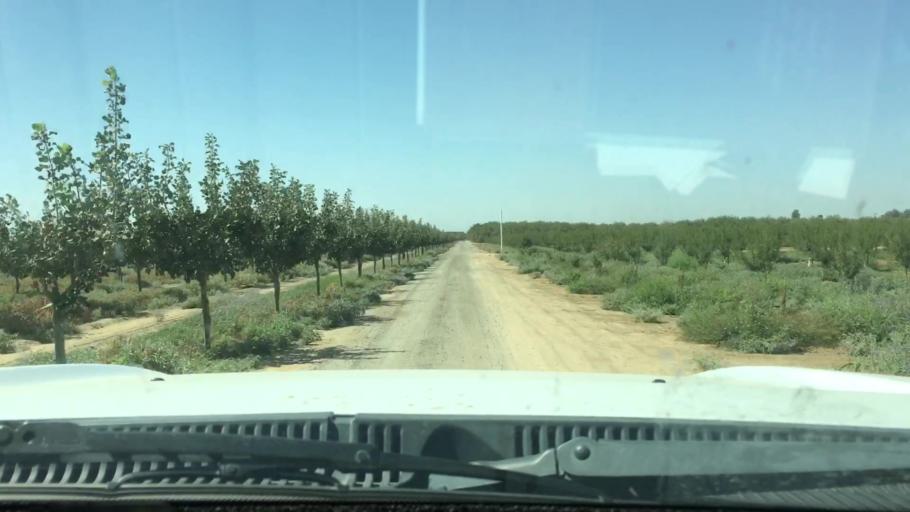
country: US
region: California
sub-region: Kern County
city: Shafter
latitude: 35.4527
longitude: -119.2889
